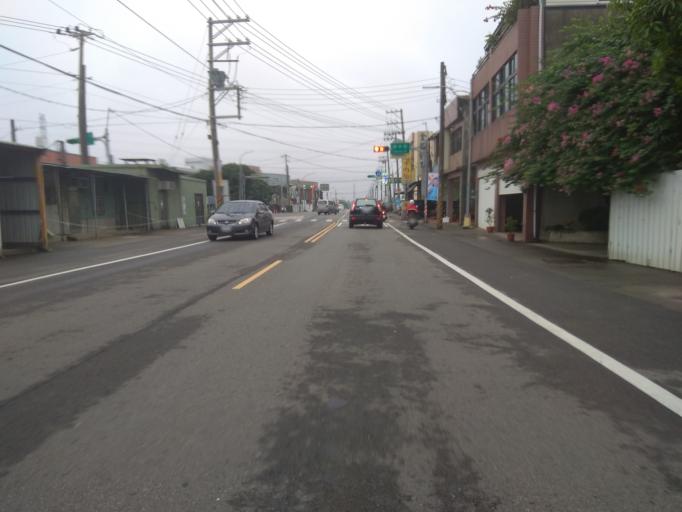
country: TW
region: Taiwan
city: Taoyuan City
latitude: 25.0153
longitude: 121.1312
